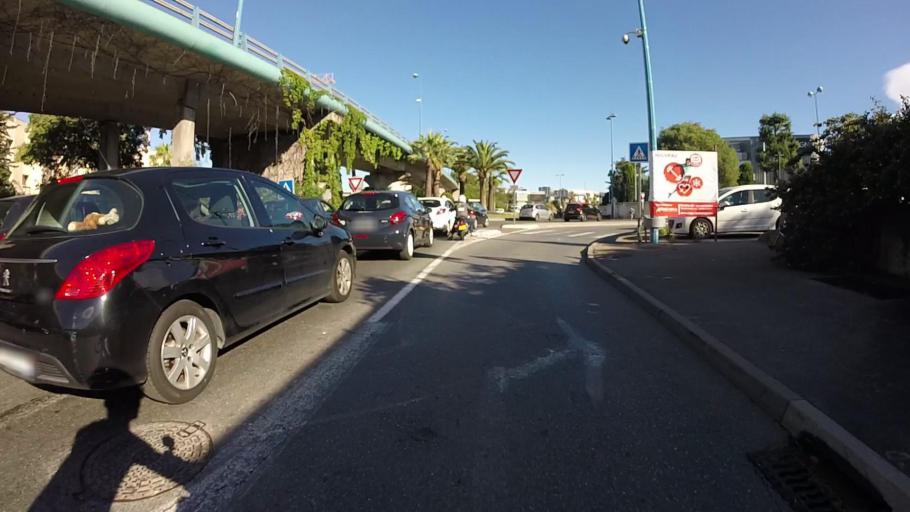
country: FR
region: Provence-Alpes-Cote d'Azur
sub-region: Departement des Alpes-Maritimes
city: Biot
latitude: 43.6013
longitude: 7.0846
